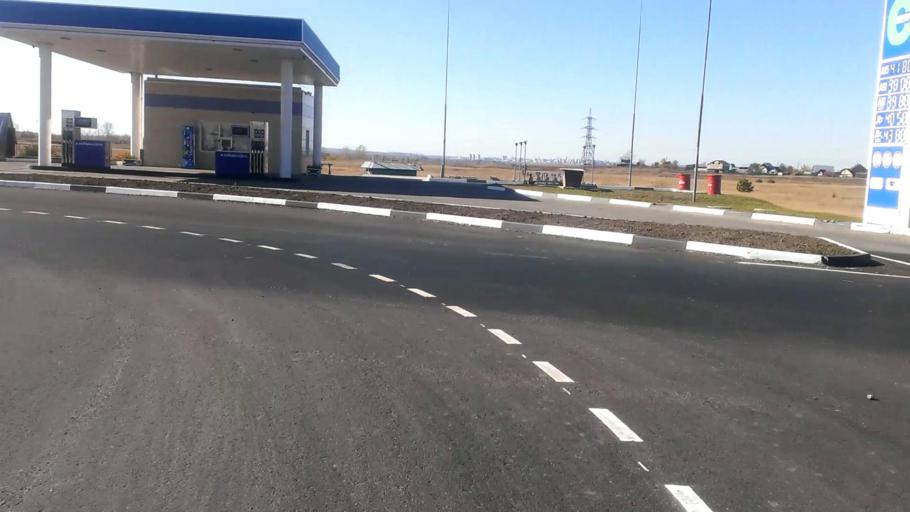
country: RU
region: Altai Krai
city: Sannikovo
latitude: 53.3368
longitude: 83.9388
